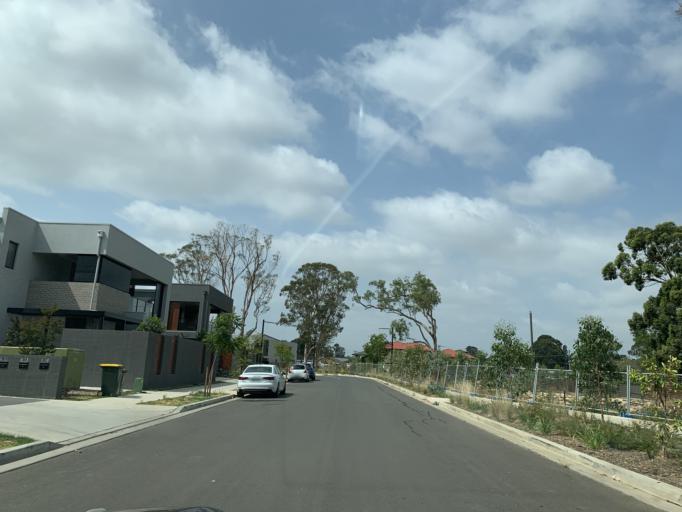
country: AU
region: New South Wales
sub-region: Blacktown
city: Blacktown
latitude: -33.7595
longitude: 150.8994
